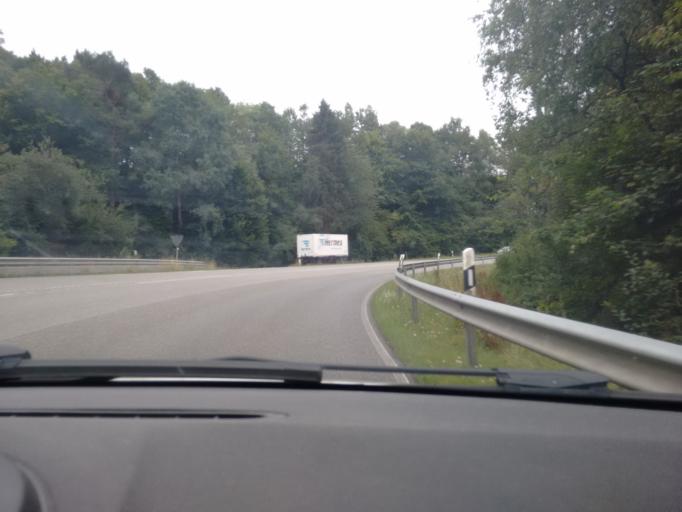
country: DE
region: Rheinland-Pfalz
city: Oberbrombach
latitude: 49.7044
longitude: 7.2611
